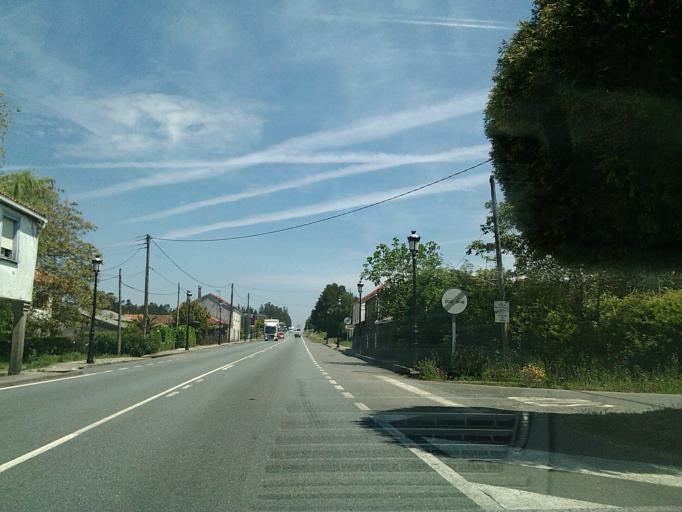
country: ES
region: Galicia
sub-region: Provincia da Coruna
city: Frades
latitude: 42.9875
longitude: -8.2916
